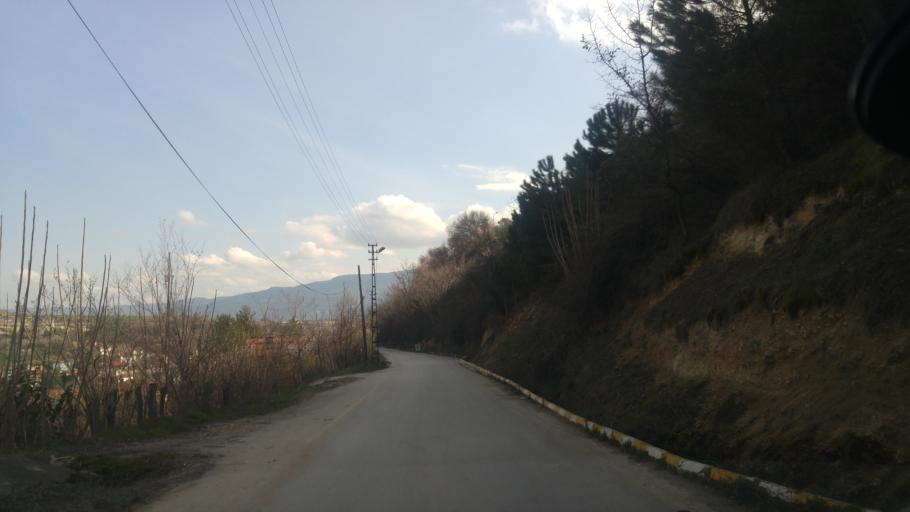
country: TR
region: Karabuk
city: Safranbolu
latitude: 41.2543
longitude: 32.6844
